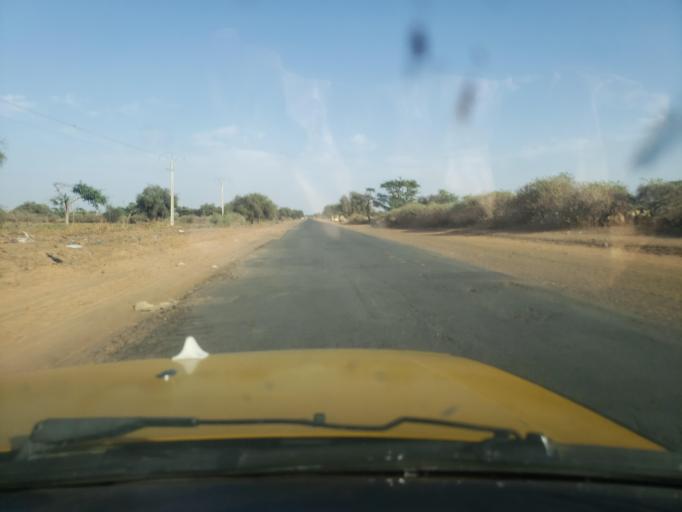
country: SN
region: Louga
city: Louga
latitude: 15.5019
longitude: -15.9425
